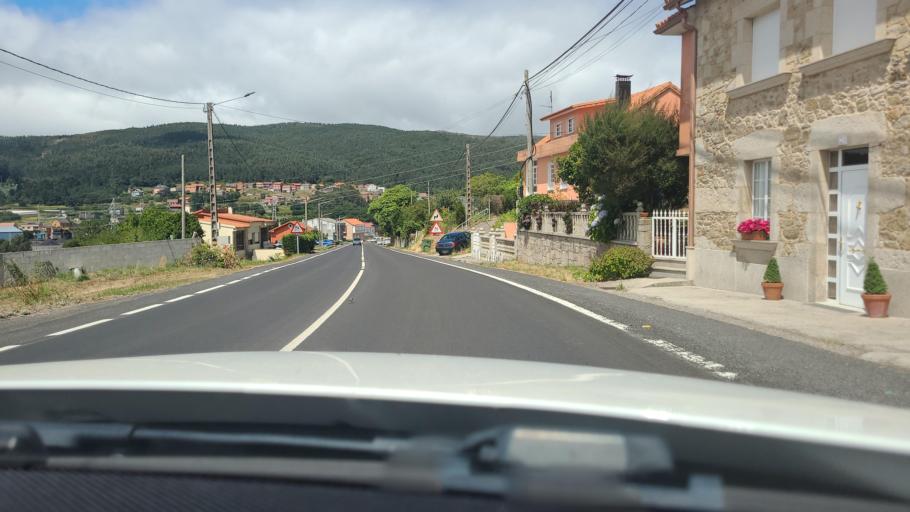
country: ES
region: Galicia
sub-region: Provincia da Coruna
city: Cee
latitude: 42.9432
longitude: -9.1718
